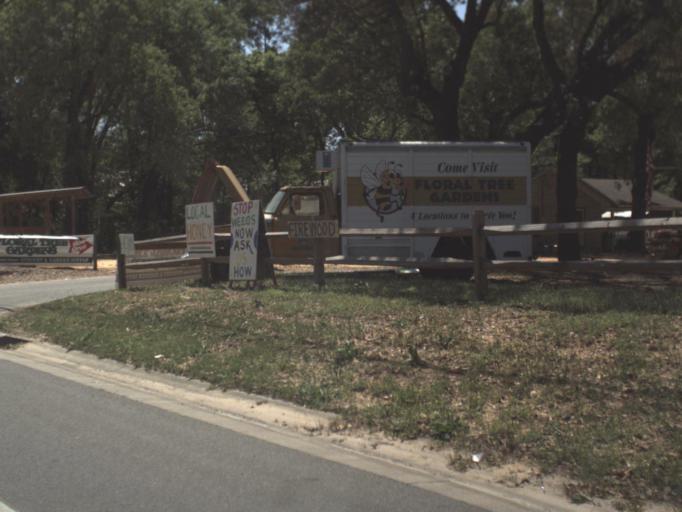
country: US
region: Florida
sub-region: Escambia County
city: Ensley
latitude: 30.5322
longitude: -87.3133
